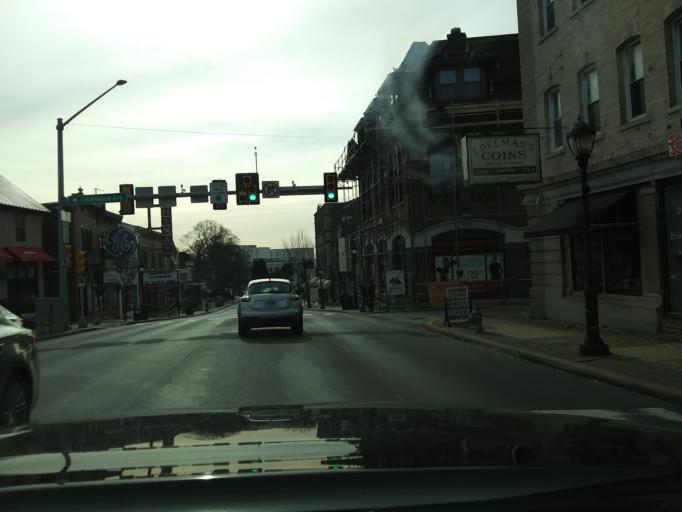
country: US
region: Pennsylvania
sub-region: Montgomery County
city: Jenkintown
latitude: 40.0953
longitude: -75.1258
